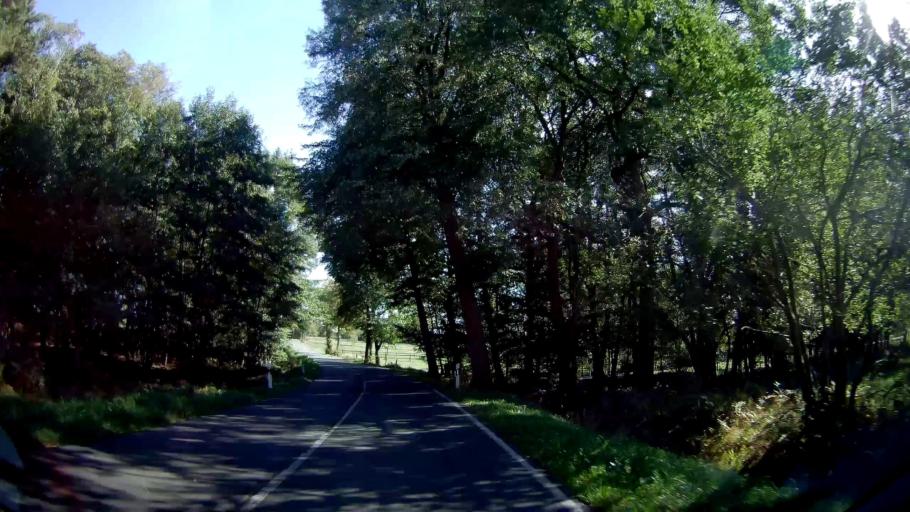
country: DE
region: North Rhine-Westphalia
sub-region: Regierungsbezirk Dusseldorf
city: Hunxe
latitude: 51.6204
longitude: 6.7910
